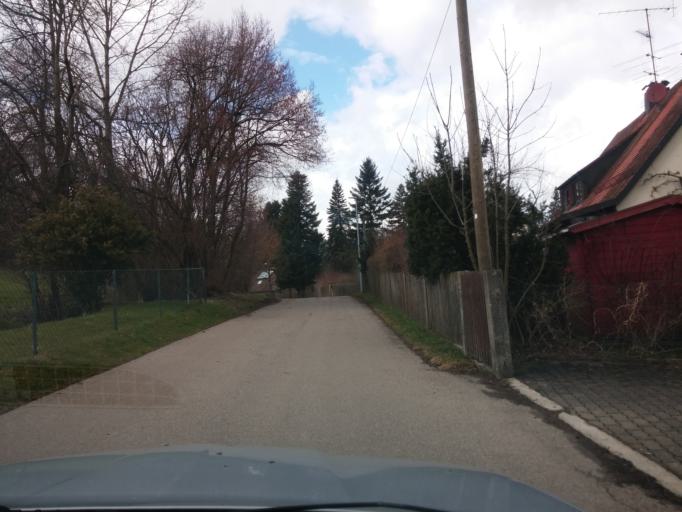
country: DE
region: Bavaria
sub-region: Swabia
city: Buxheim
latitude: 47.9777
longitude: 10.1463
